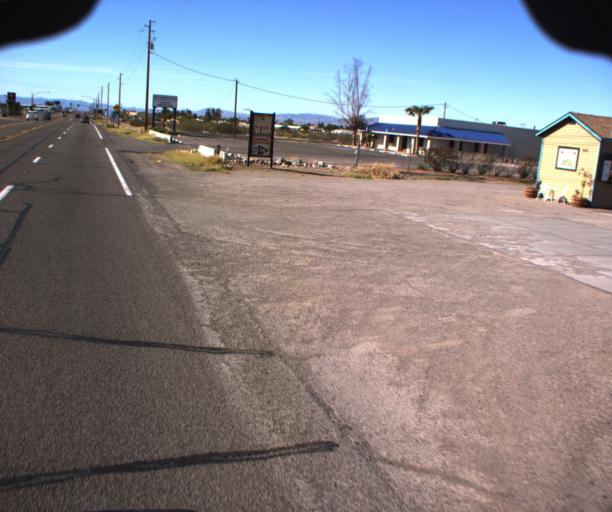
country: US
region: Arizona
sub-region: Mohave County
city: Mohave Valley
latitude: 34.9997
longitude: -114.5981
